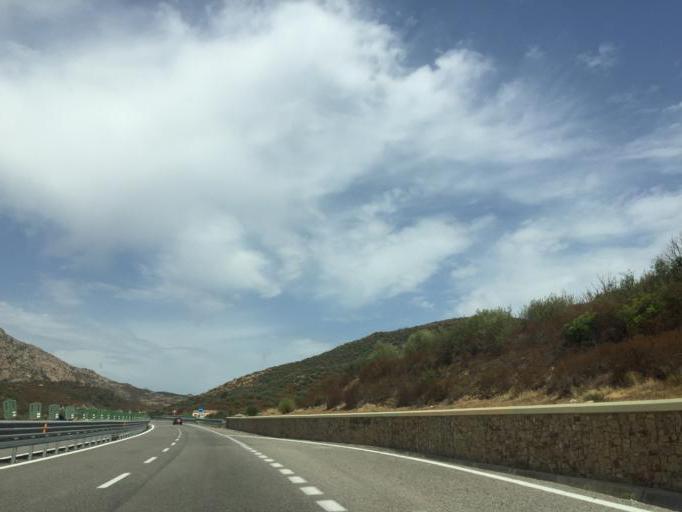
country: IT
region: Sardinia
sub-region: Provincia di Olbia-Tempio
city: San Teodoro
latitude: 40.7710
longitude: 9.6357
